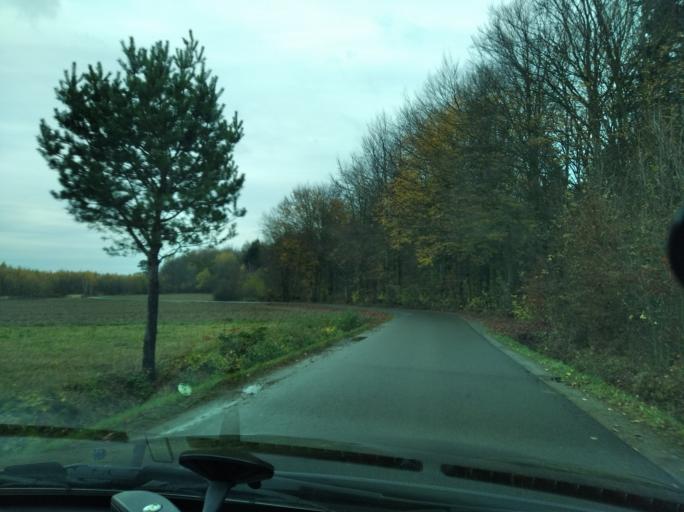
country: PL
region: Subcarpathian Voivodeship
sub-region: Powiat strzyzowski
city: Strzyzow
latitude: 49.9097
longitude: 21.7747
